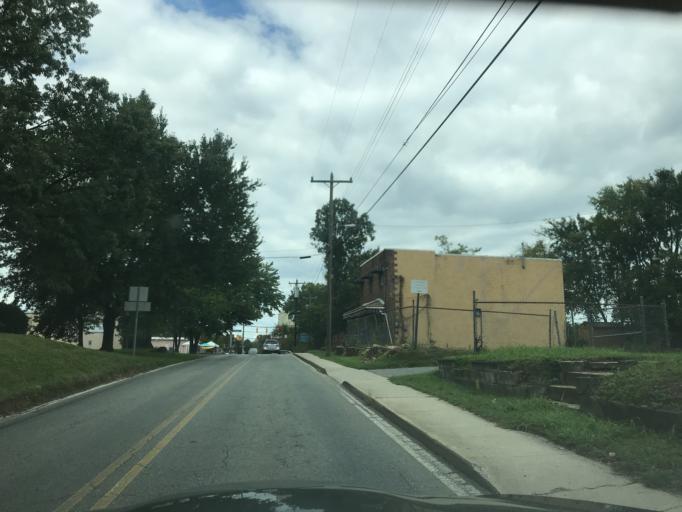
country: US
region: North Carolina
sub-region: Orange County
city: Chapel Hill
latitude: 35.9084
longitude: -79.0644
